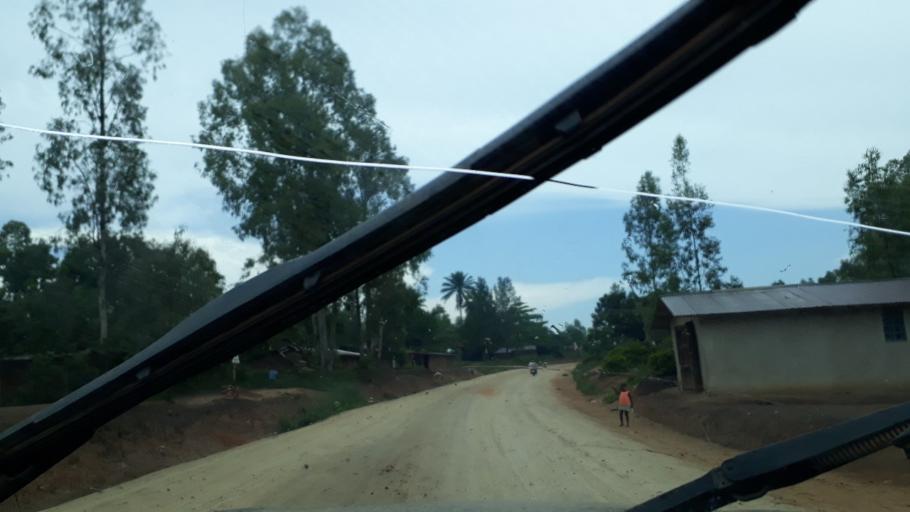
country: CD
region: Eastern Province
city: Bunia
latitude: 1.5993
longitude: 30.2658
